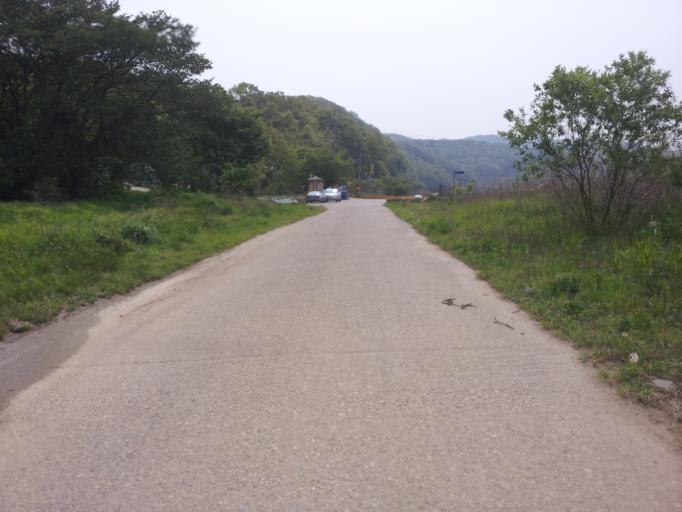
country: KR
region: Daejeon
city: Daejeon
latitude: 36.2716
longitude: 127.3395
